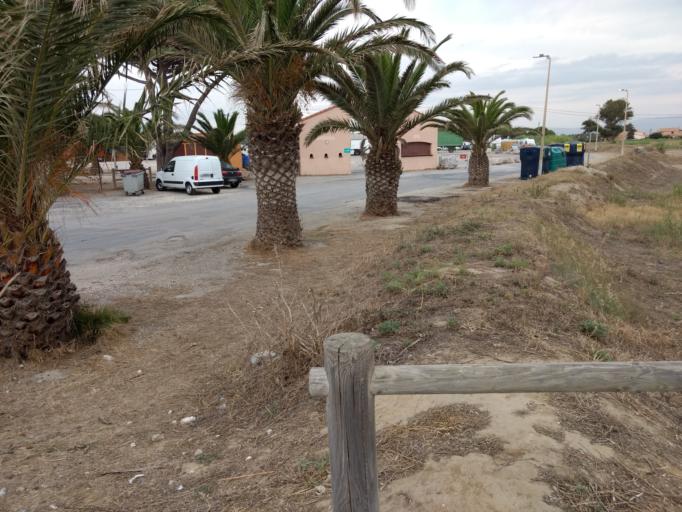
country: FR
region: Languedoc-Roussillon
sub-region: Departement des Pyrenees-Orientales
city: Le Barcares
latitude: 42.7830
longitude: 3.0335
